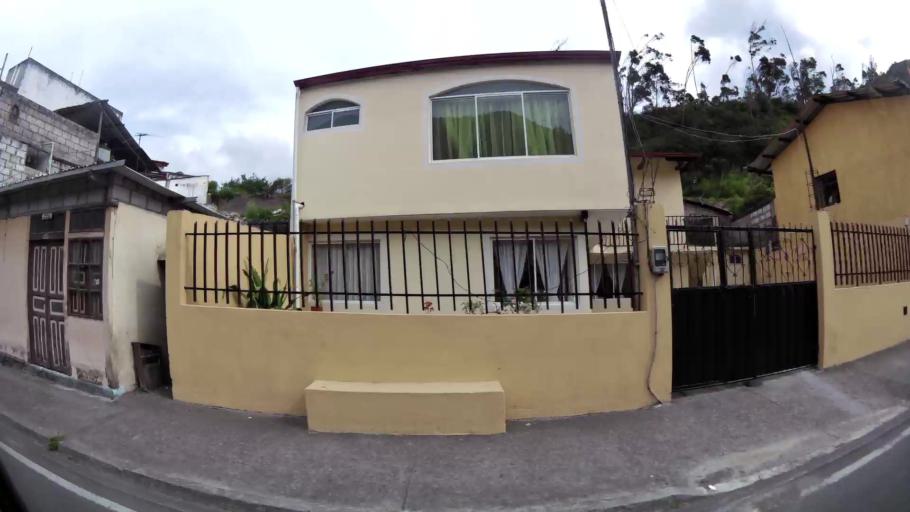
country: EC
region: Tungurahua
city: Banos
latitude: -1.3976
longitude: -78.4332
